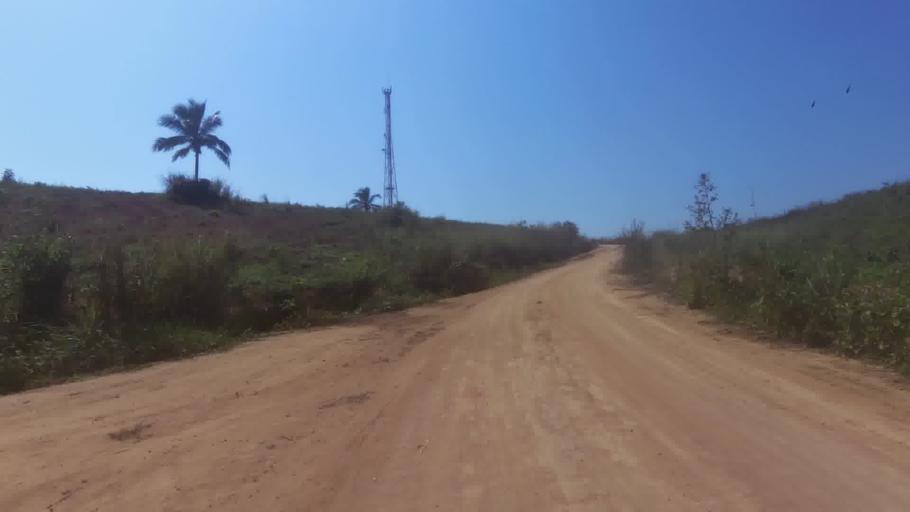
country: BR
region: Espirito Santo
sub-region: Marataizes
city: Marataizes
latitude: -21.1026
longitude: -40.8524
